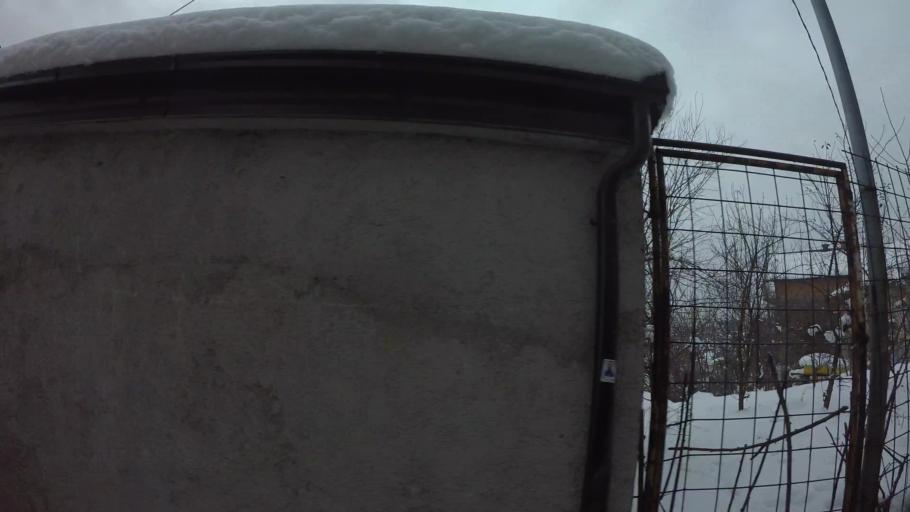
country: BA
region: Federation of Bosnia and Herzegovina
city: Kobilja Glava
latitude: 43.8669
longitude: 18.4375
